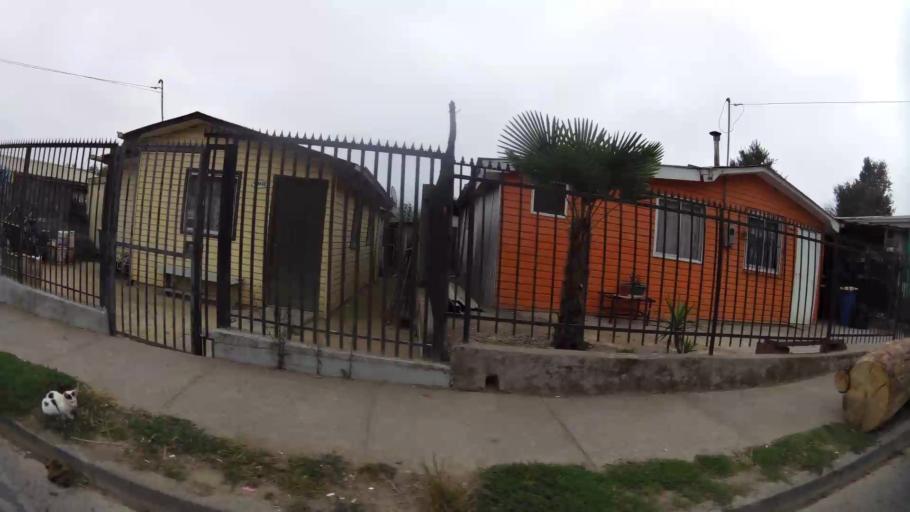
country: CL
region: Biobio
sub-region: Provincia de Concepcion
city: Concepcion
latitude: -36.8176
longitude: -72.9864
